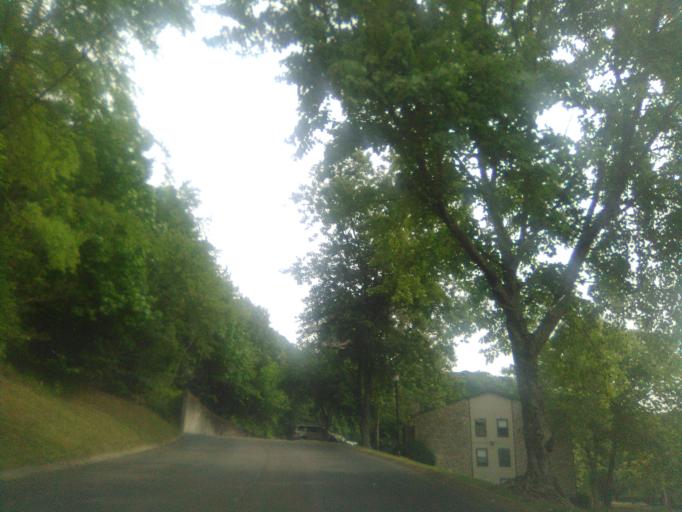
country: US
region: Tennessee
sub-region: Davidson County
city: Belle Meade
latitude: 36.0838
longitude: -86.9086
